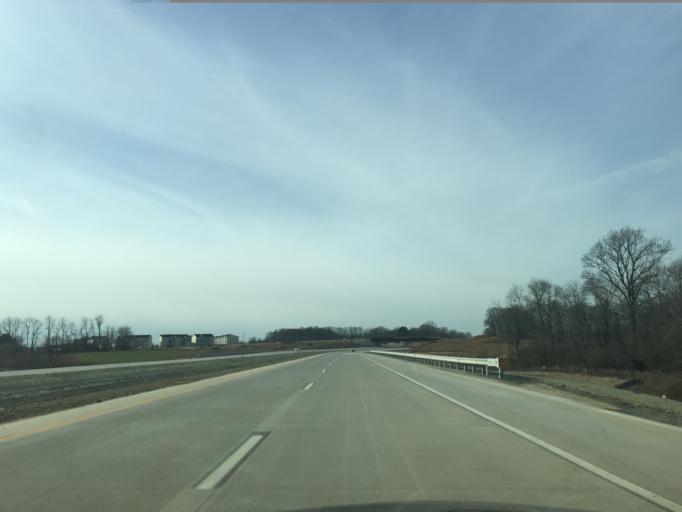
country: US
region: Delaware
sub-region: New Castle County
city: Delaware City
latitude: 39.5259
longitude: -75.6574
